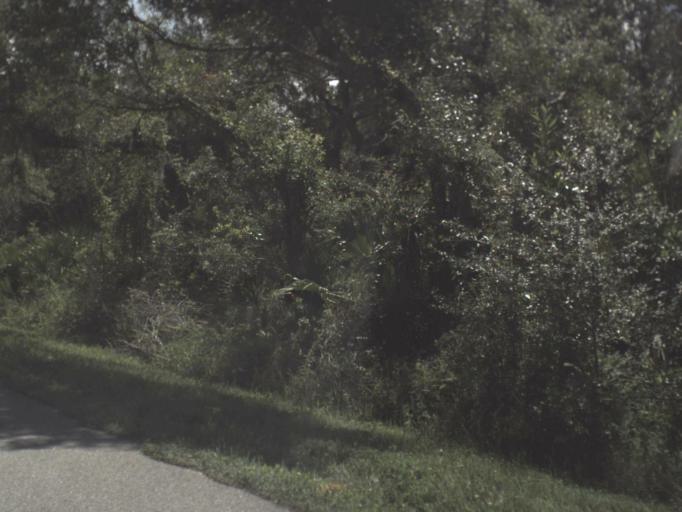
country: US
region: Florida
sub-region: Sarasota County
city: Lake Sarasota
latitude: 27.3673
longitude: -82.2106
